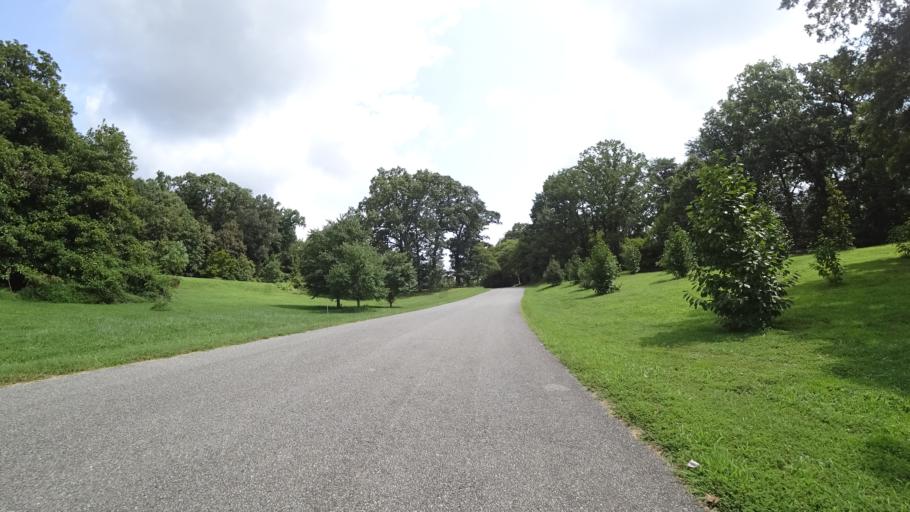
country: US
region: Maryland
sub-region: Prince George's County
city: Colmar Manor
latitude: 38.9110
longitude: -76.9577
